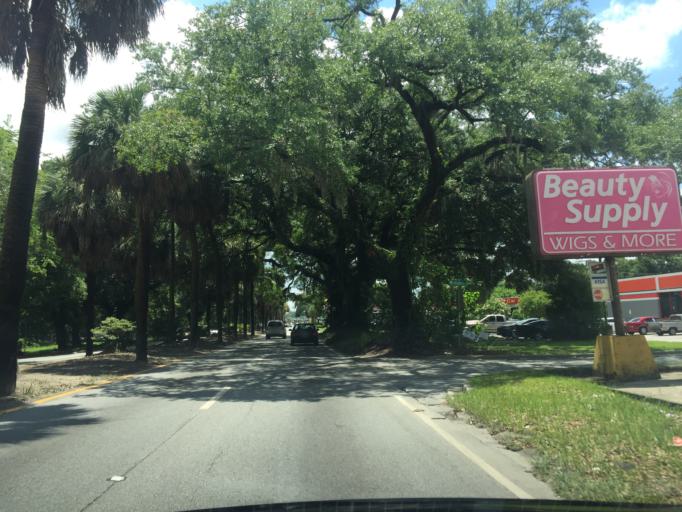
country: US
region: Georgia
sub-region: Chatham County
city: Thunderbolt
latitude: 32.0456
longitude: -81.0760
